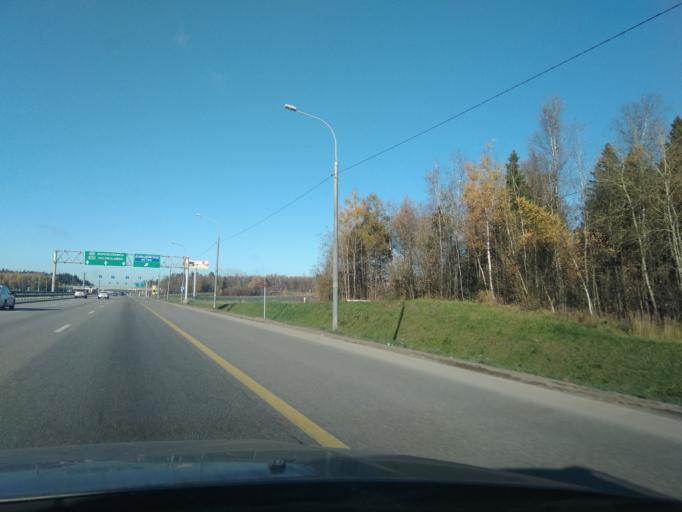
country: RU
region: Moskovskaya
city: Istra
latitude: 55.8508
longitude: 36.7950
